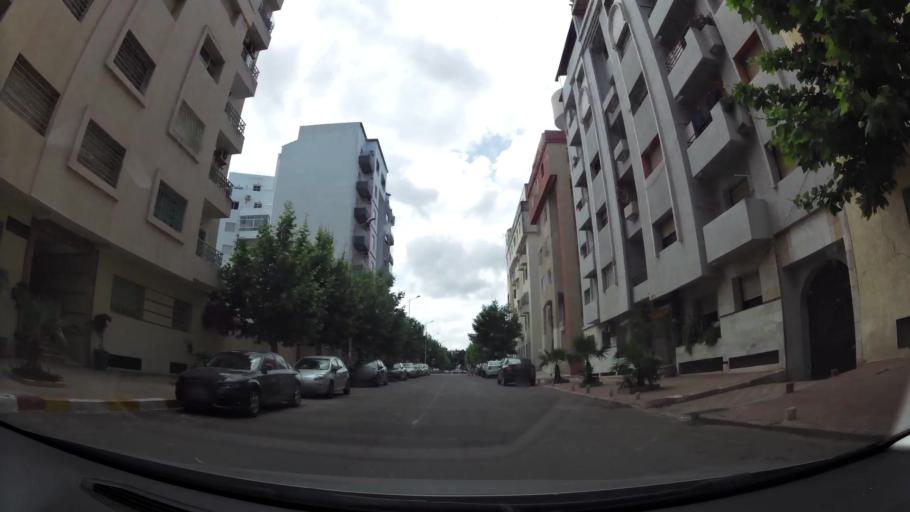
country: MA
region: Gharb-Chrarda-Beni Hssen
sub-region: Kenitra Province
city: Kenitra
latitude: 34.2549
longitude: -6.5864
